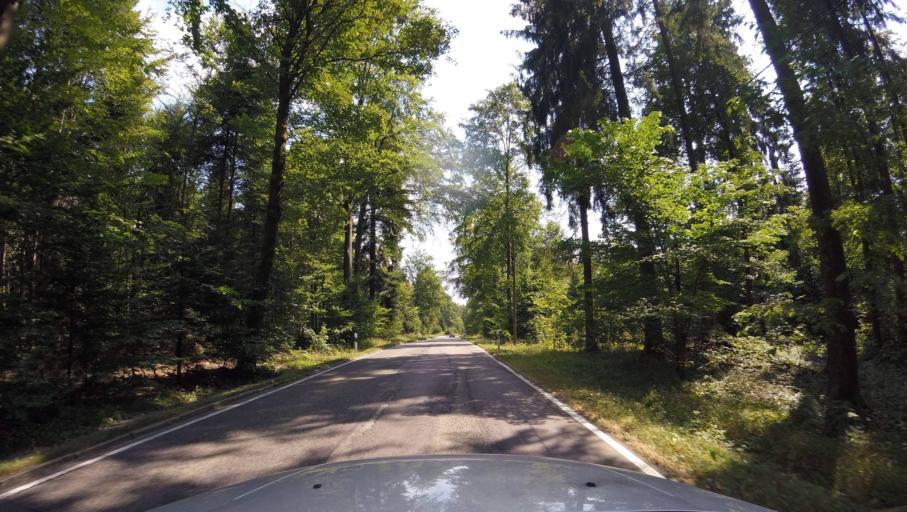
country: DE
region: Baden-Wuerttemberg
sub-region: Regierungsbezirk Stuttgart
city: Kaisersbach
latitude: 48.9286
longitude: 9.6190
